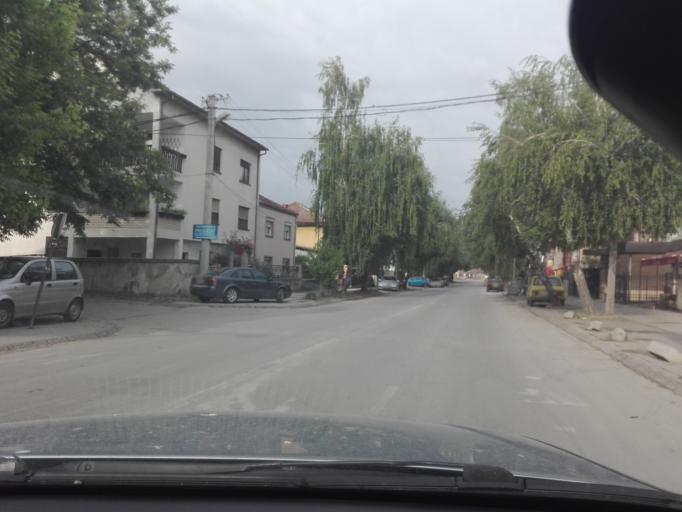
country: MK
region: Bitola
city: Bitola
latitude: 41.0236
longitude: 21.3394
